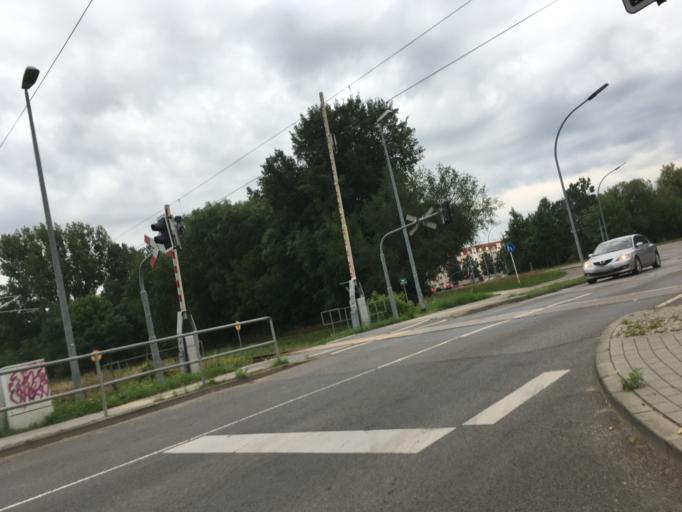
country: DE
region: Brandenburg
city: Schwedt (Oder)
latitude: 53.0661
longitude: 14.2794
